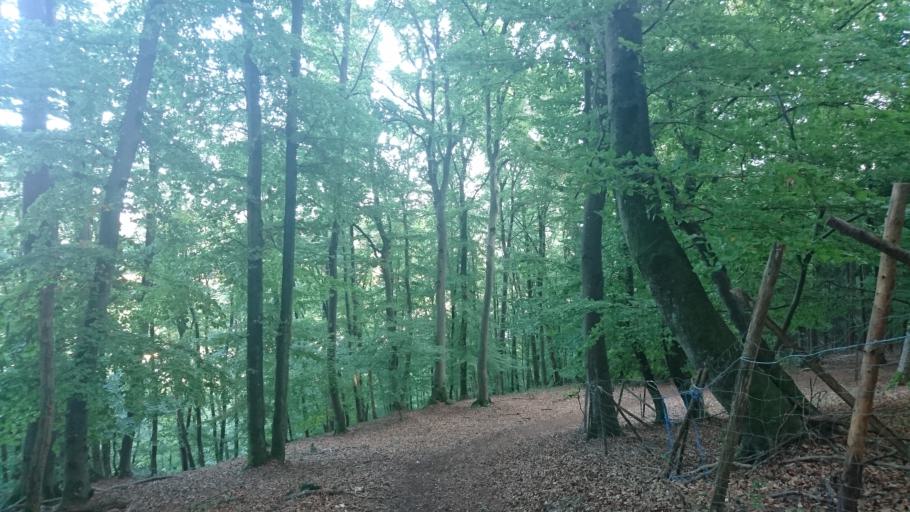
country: DE
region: Bavaria
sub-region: Regierungsbezirk Mittelfranken
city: Treuchtlingen
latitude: 48.9733
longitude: 10.9027
